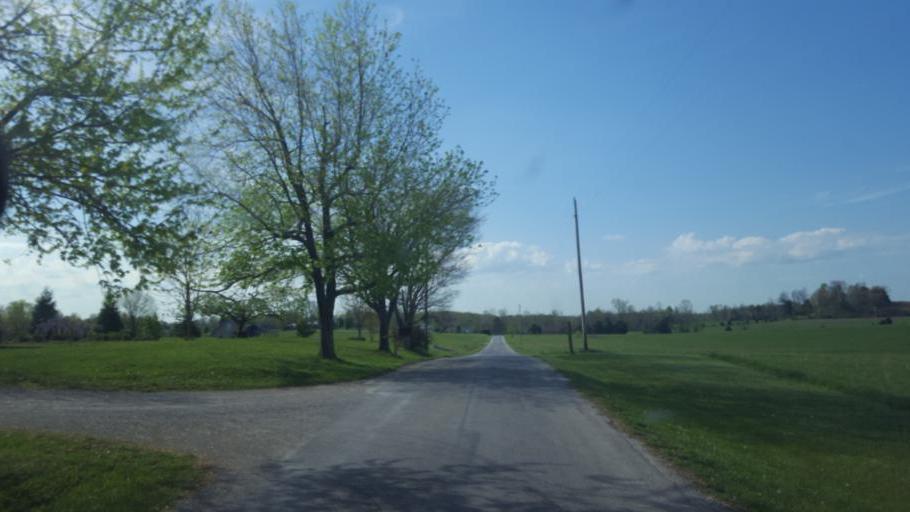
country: US
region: Kentucky
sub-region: Hart County
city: Munfordville
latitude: 37.3223
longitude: -86.0950
